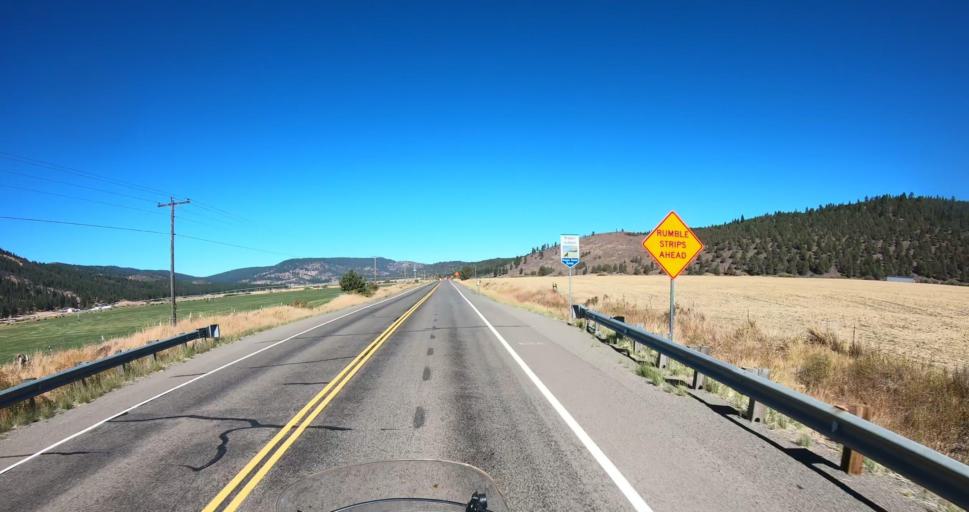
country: US
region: Oregon
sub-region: Lake County
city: Lakeview
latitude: 42.3401
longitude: -120.2975
